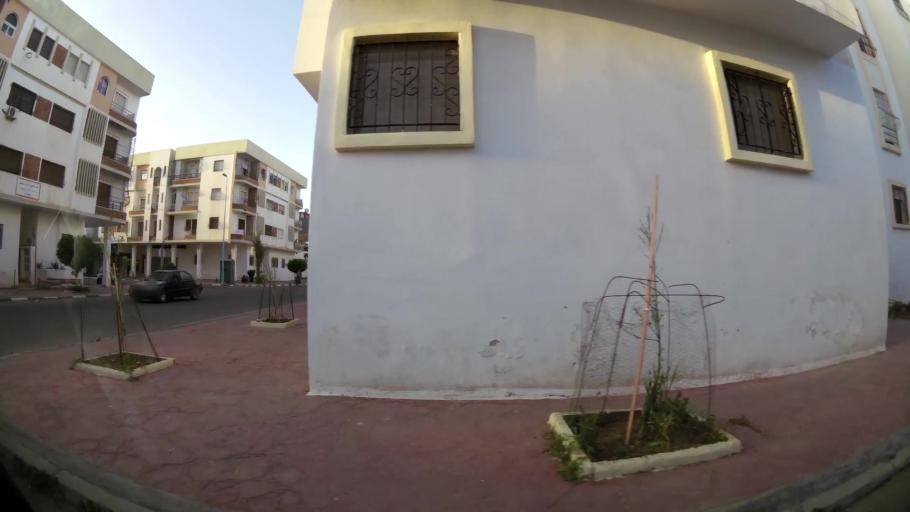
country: MA
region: Oued ed Dahab-Lagouira
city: Dakhla
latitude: 30.3982
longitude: -9.5610
